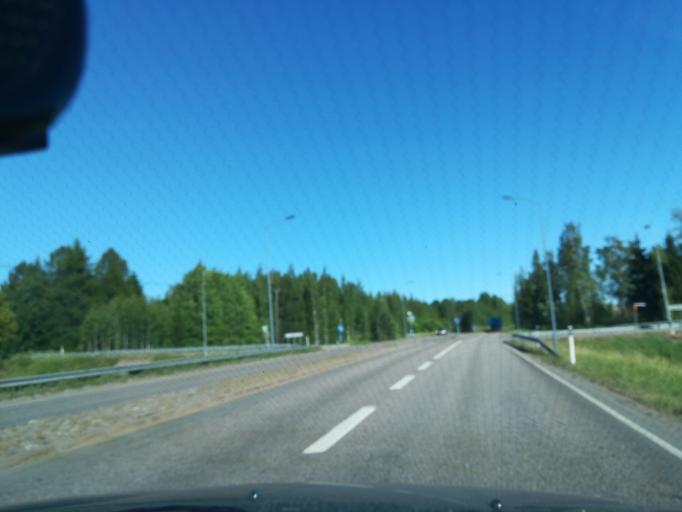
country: FI
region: South Karelia
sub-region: Imatra
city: Imatra
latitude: 61.1551
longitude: 28.8020
